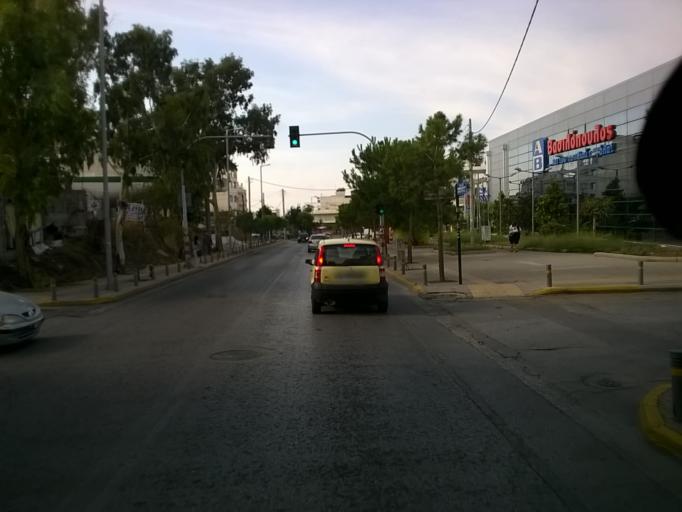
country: GR
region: Attica
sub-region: Nomarchia Athinas
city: Alimos
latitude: 37.9192
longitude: 23.7206
